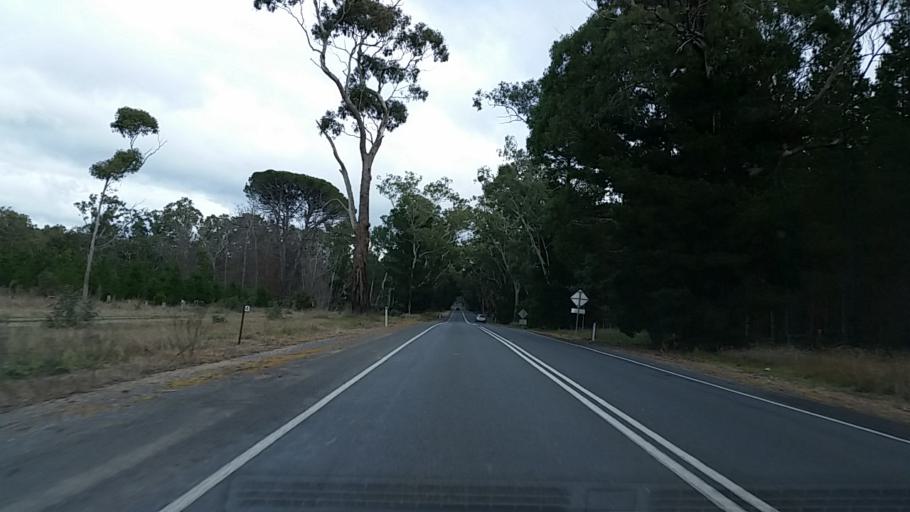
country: AU
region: South Australia
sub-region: Mount Barker
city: Meadows
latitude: -35.2070
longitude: 138.7077
